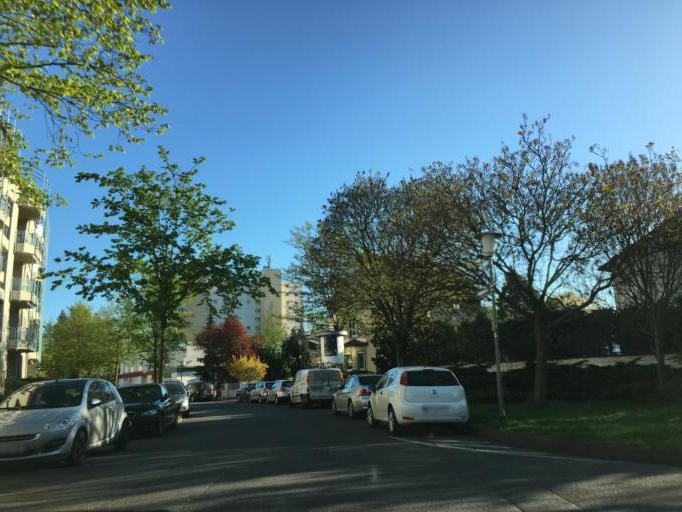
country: DE
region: Hesse
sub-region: Regierungsbezirk Darmstadt
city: Offenbach
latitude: 50.0996
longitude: 8.7786
